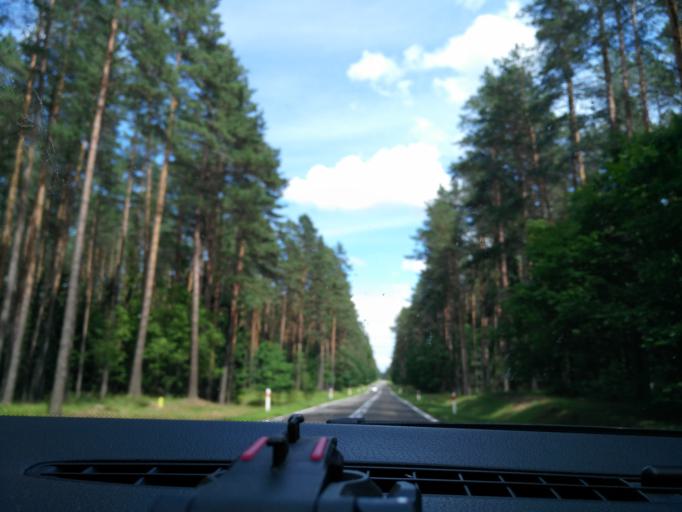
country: PL
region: Podlasie
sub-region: Powiat sejnenski
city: Sejny
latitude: 53.9754
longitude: 23.2694
